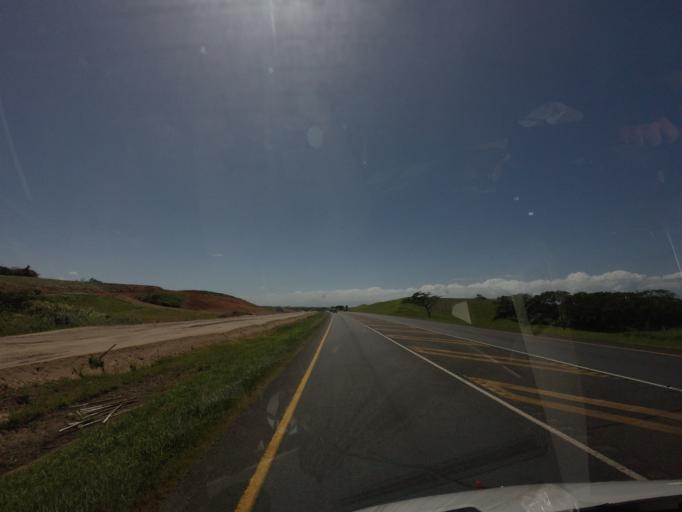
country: ZA
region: KwaZulu-Natal
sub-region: uThungulu District Municipality
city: eSikhawini
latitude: -28.9310
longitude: 31.7762
